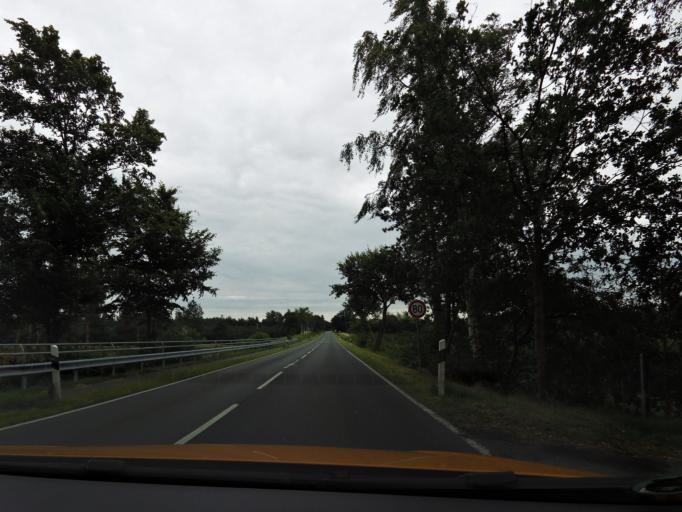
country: DE
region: Lower Saxony
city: Westerstede
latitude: 53.2511
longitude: 7.9715
